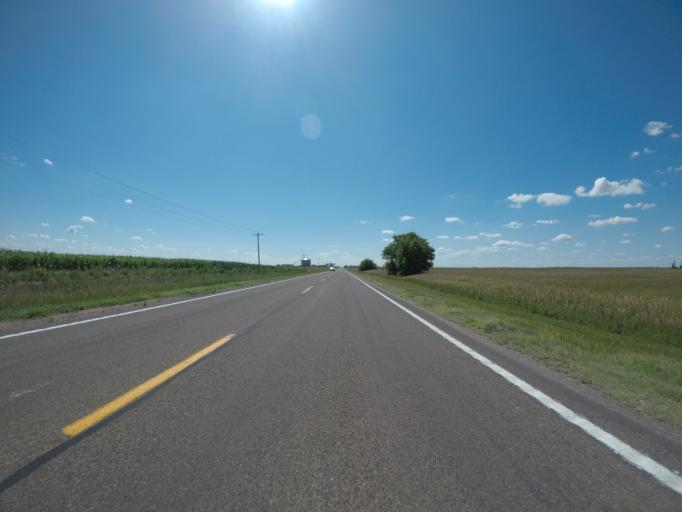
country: US
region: Nebraska
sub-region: Chase County
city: Imperial
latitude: 40.5376
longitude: -101.7737
